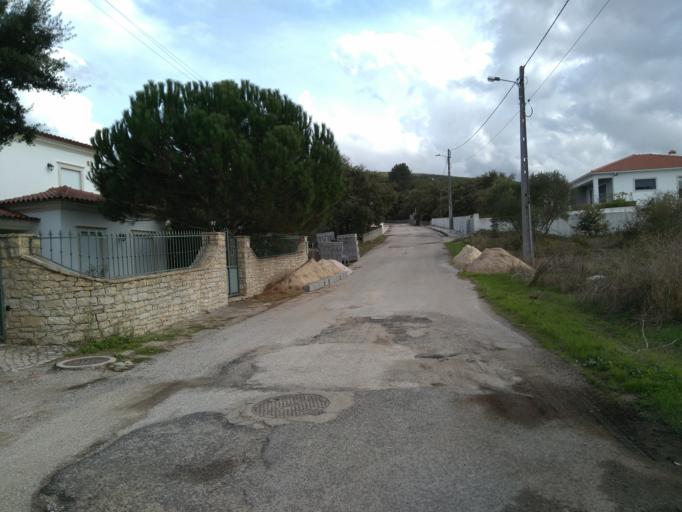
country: PT
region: Leiria
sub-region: Porto de Mos
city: Porto de Mos
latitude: 39.5962
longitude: -8.8075
